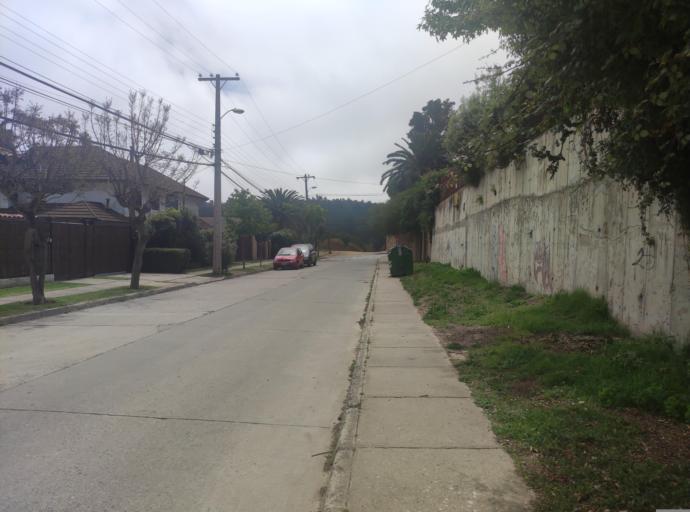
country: CL
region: Valparaiso
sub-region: Provincia de Valparaiso
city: Vina del Mar
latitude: -32.9687
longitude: -71.5261
